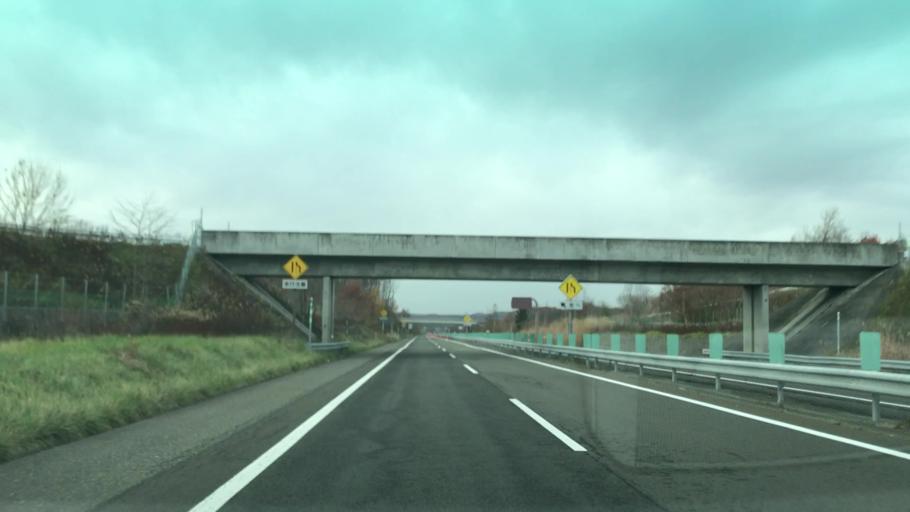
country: JP
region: Hokkaido
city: Chitose
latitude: 42.8930
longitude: 141.8107
